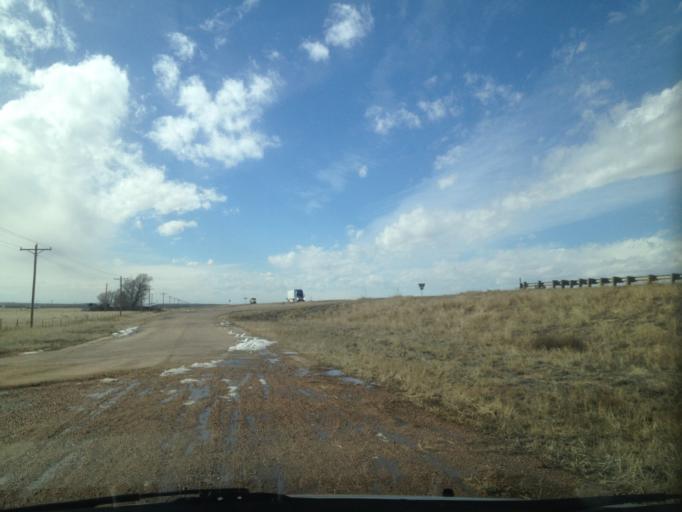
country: US
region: Colorado
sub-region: Weld County
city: Kersey
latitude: 40.2909
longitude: -104.2554
